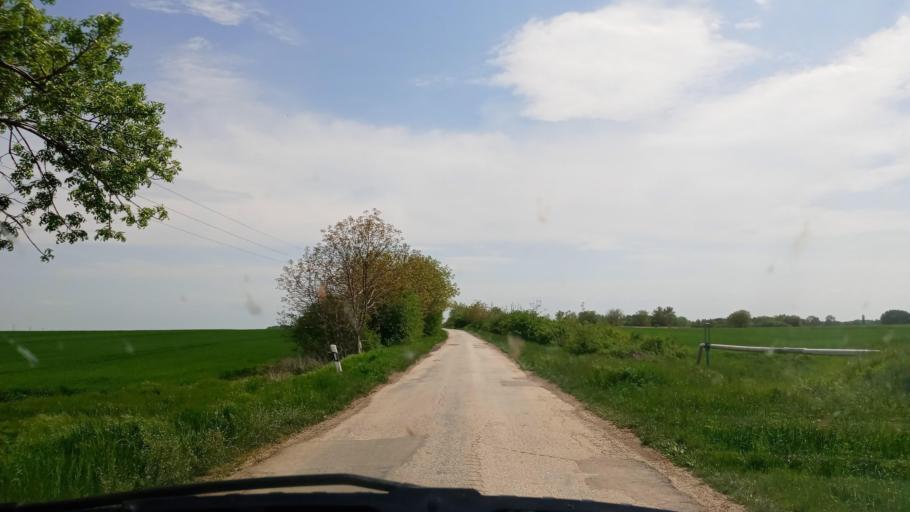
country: HU
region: Baranya
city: Villany
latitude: 45.8191
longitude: 18.5077
